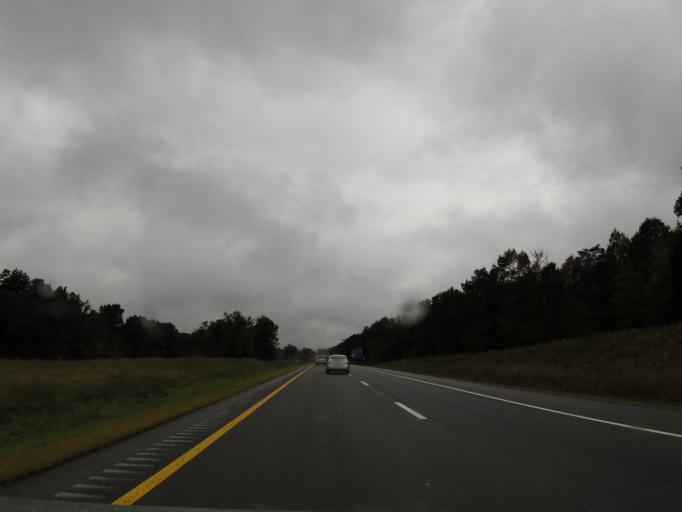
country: US
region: Tennessee
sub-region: Bradley County
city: Hopewell
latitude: 35.2422
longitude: -84.8462
